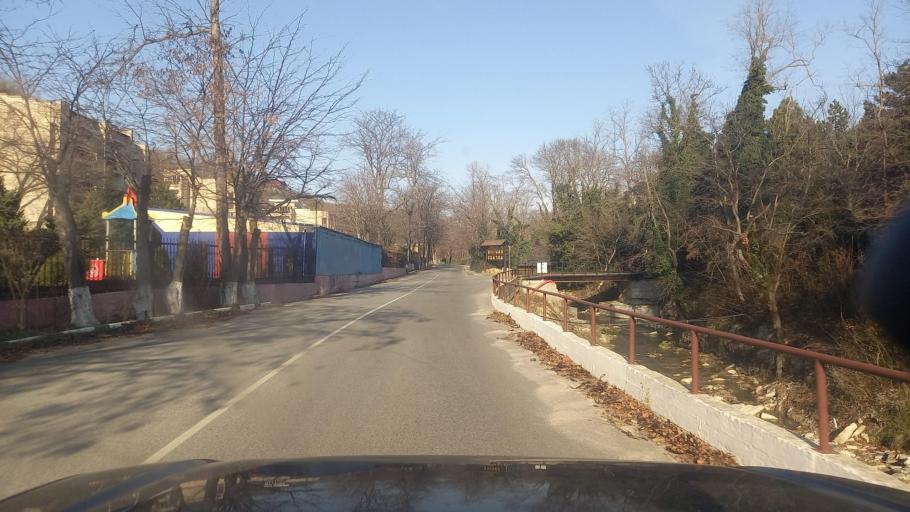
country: RU
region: Krasnodarskiy
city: Myskhako
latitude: 44.6612
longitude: 37.6846
